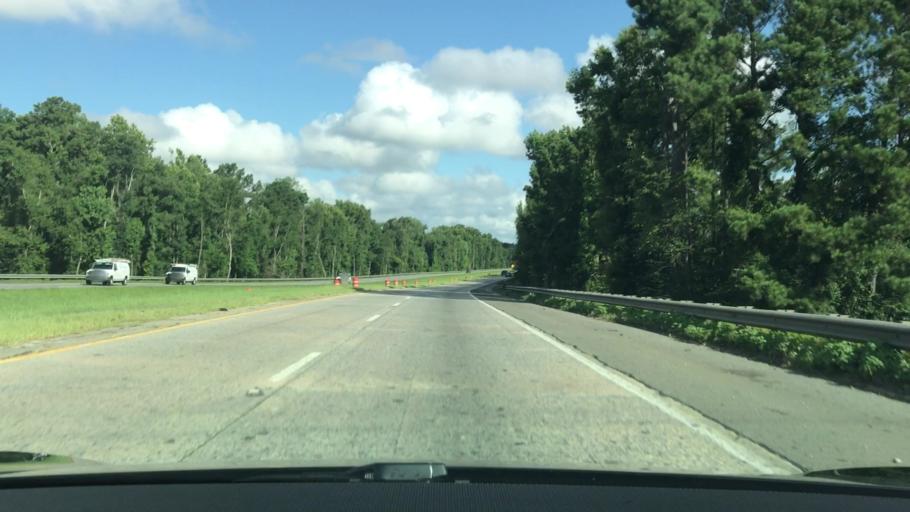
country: US
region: Georgia
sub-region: Bibb County
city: Macon
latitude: 32.8258
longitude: -83.5996
